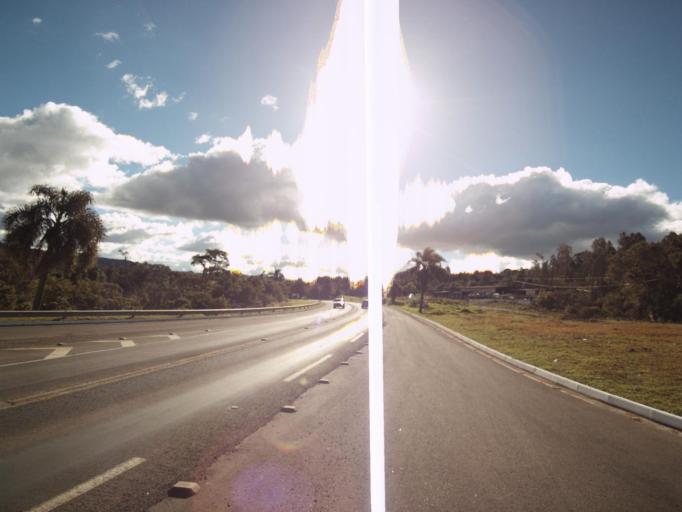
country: BR
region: Santa Catarina
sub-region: Joacaba
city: Joacaba
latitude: -27.1672
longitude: -51.5603
